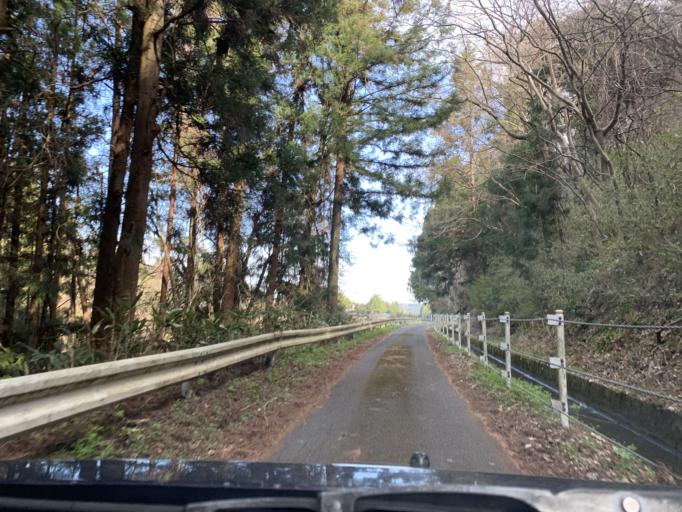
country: JP
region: Iwate
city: Ichinoseki
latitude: 38.9321
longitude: 141.0753
